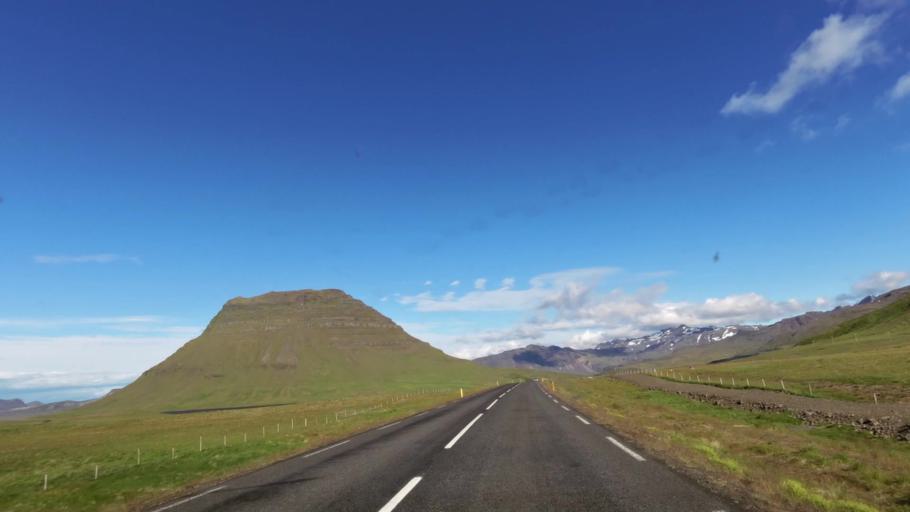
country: IS
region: West
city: Olafsvik
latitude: 64.9399
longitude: -23.3644
